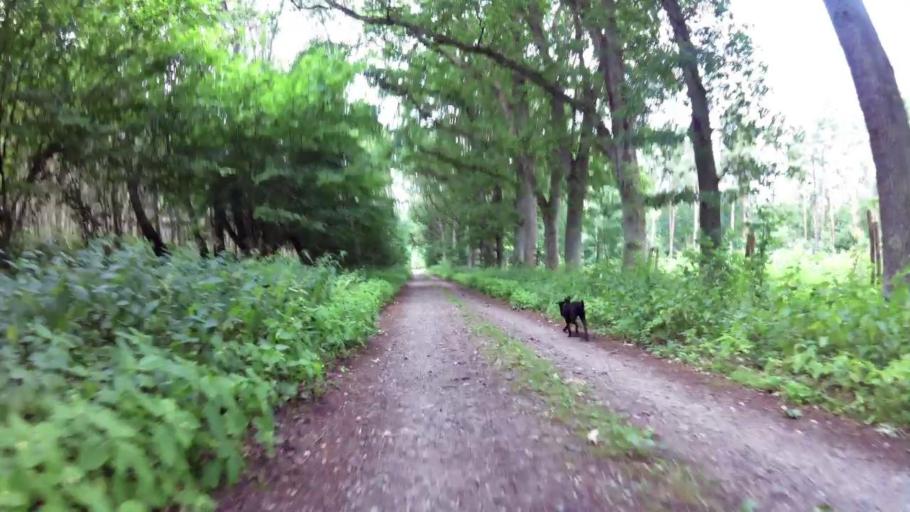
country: PL
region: West Pomeranian Voivodeship
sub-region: Powiat lobeski
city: Lobez
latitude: 53.7534
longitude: 15.5983
